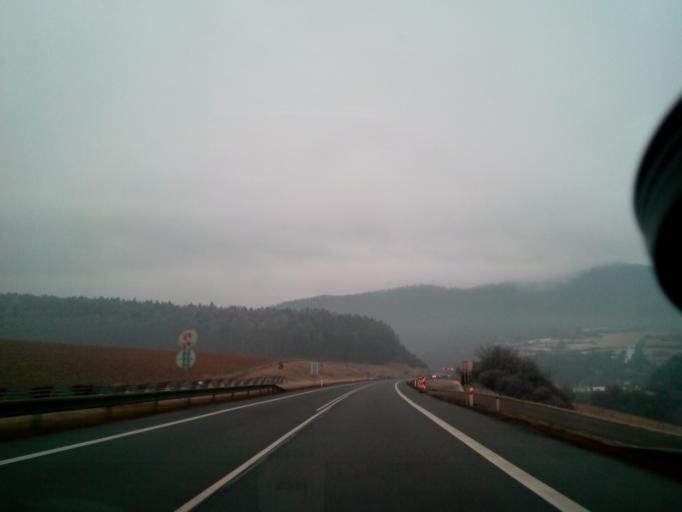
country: SK
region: Presovsky
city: Spisske Podhradie
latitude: 49.0095
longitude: 20.8246
